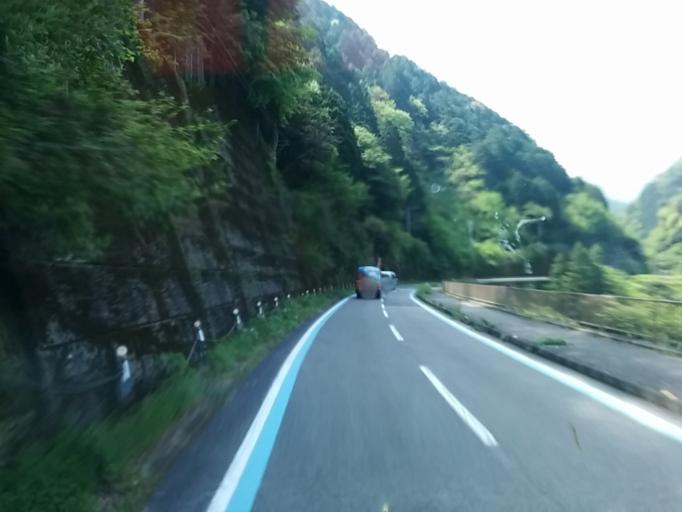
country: JP
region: Ehime
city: Niihama
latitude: 33.8915
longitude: 133.3102
